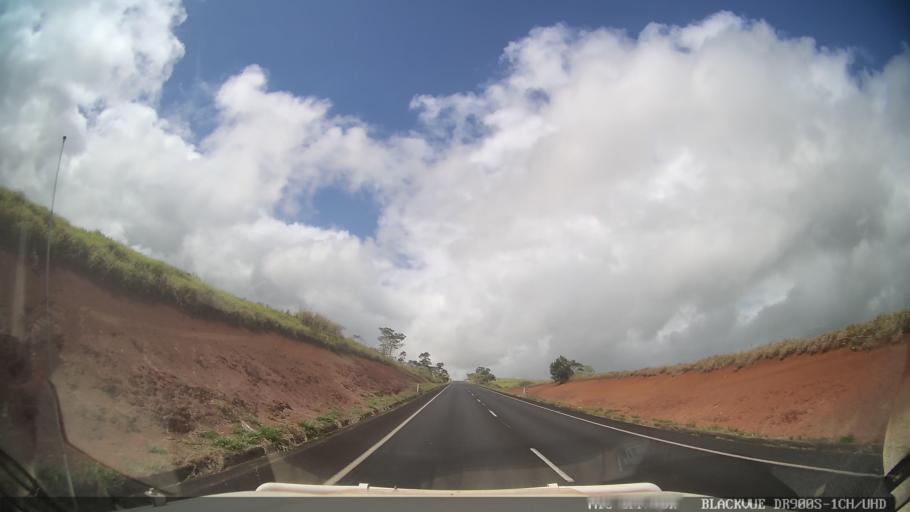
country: AU
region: Queensland
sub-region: Tablelands
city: Atherton
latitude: -17.2948
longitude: 145.6179
